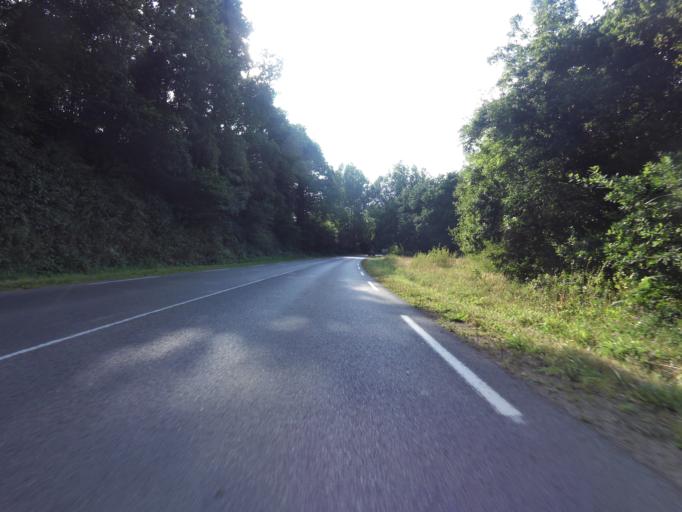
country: FR
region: Brittany
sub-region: Departement du Finistere
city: Pouldreuzic
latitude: 47.9701
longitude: -4.3808
